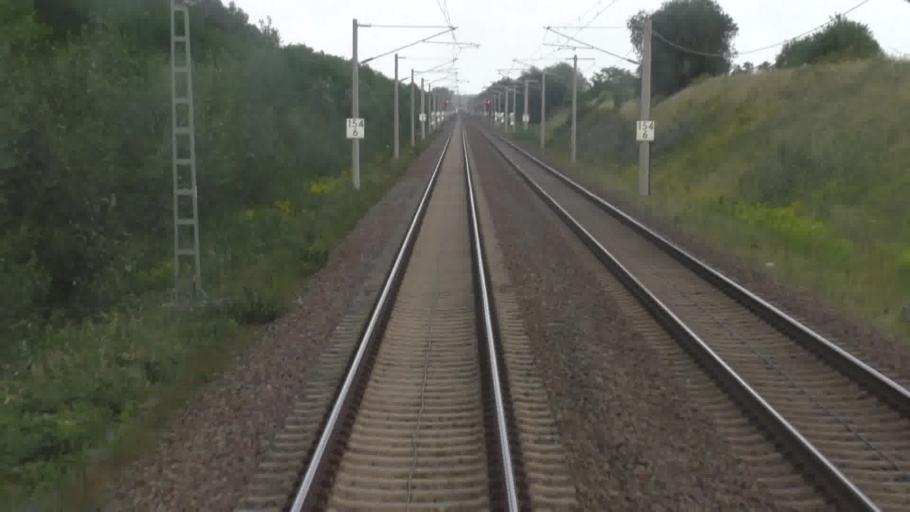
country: DE
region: Brandenburg
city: Kotzen
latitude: 52.5943
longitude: 12.5931
